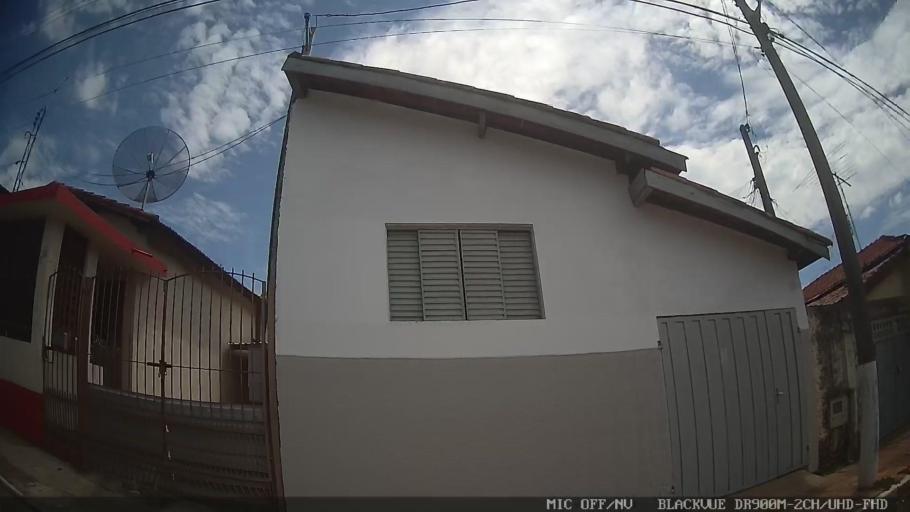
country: BR
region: Sao Paulo
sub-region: Laranjal Paulista
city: Laranjal Paulista
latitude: -23.0418
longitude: -47.8345
